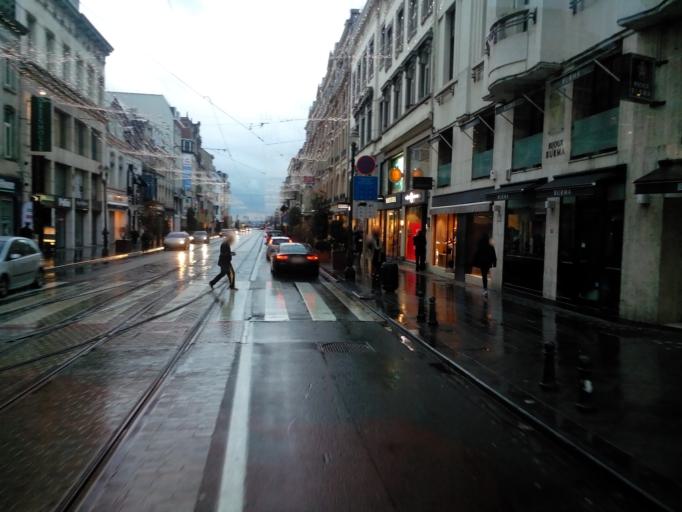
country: BE
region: Brussels Capital
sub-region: Bruxelles-Capitale
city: Brussels
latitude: 50.8337
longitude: 4.3573
